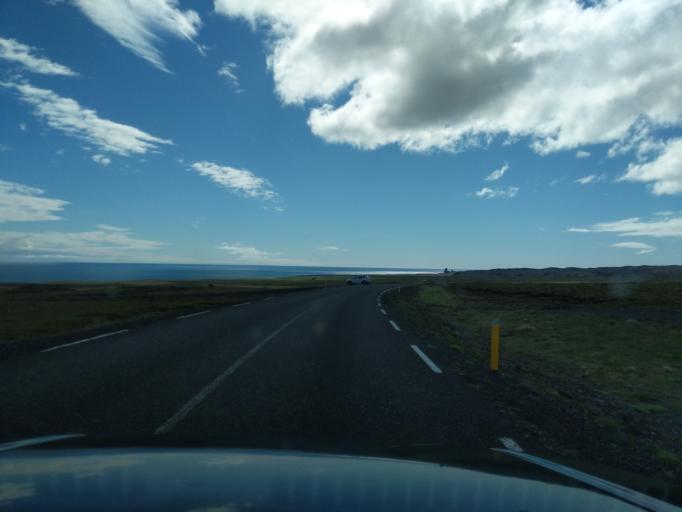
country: IS
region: West
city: Olafsvik
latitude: 64.7576
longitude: -23.6912
